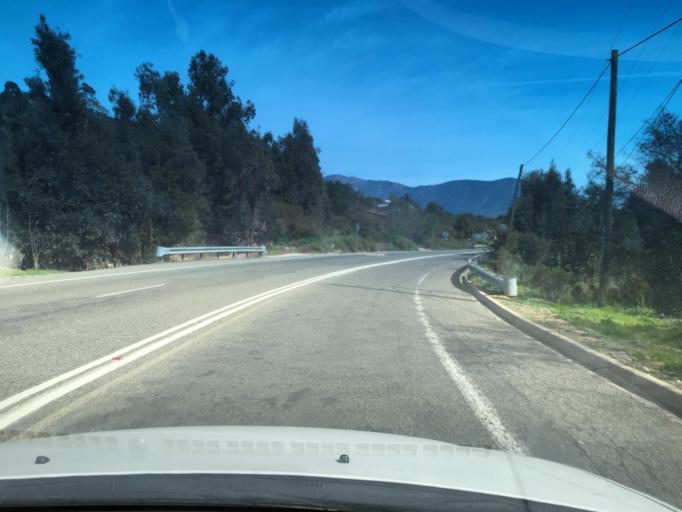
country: CL
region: Valparaiso
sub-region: Provincia de San Felipe
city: Llaillay
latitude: -33.0600
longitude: -71.0358
